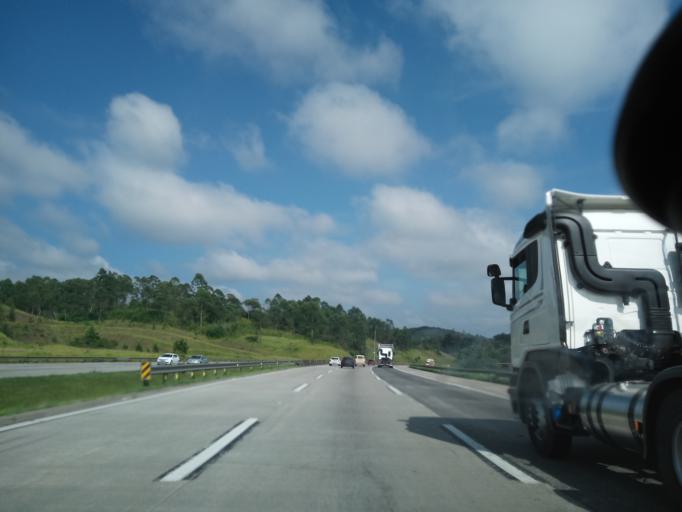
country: BR
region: Sao Paulo
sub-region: Itapecerica Da Serra
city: Itapecerica da Serra
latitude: -23.7484
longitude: -46.8078
